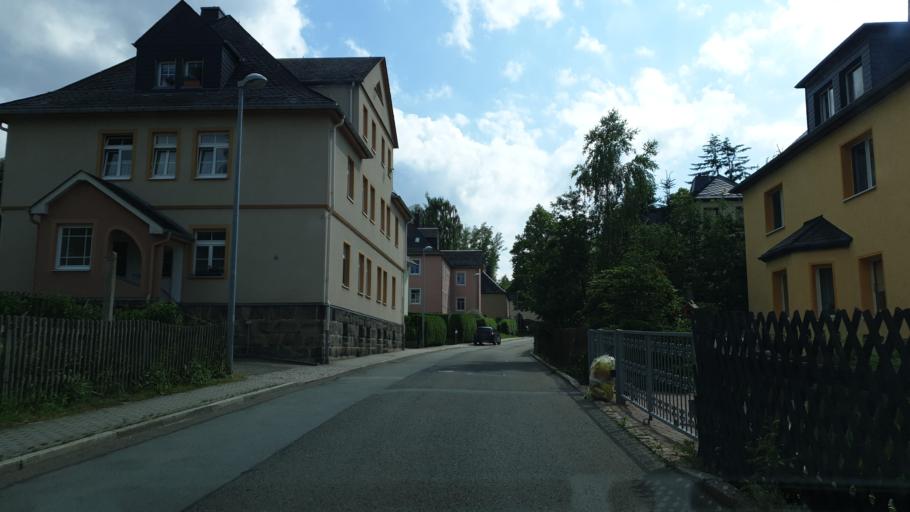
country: DE
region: Saxony
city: Lugau
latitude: 50.7367
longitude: 12.7420
